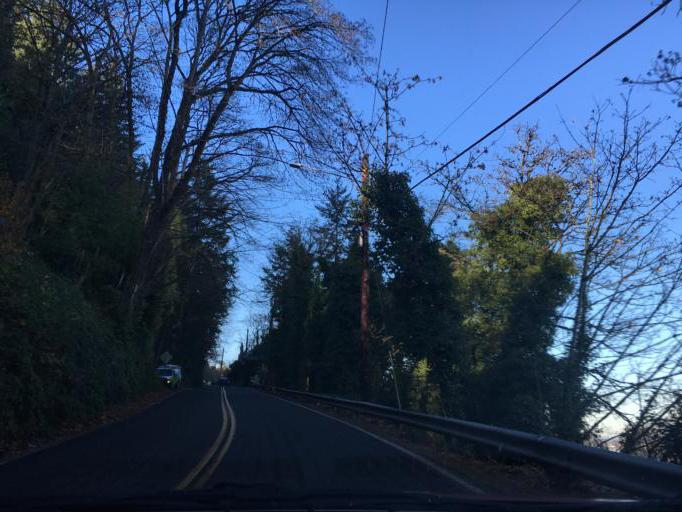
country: US
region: Oregon
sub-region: Washington County
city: West Haven
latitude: 45.5866
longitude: -122.7731
